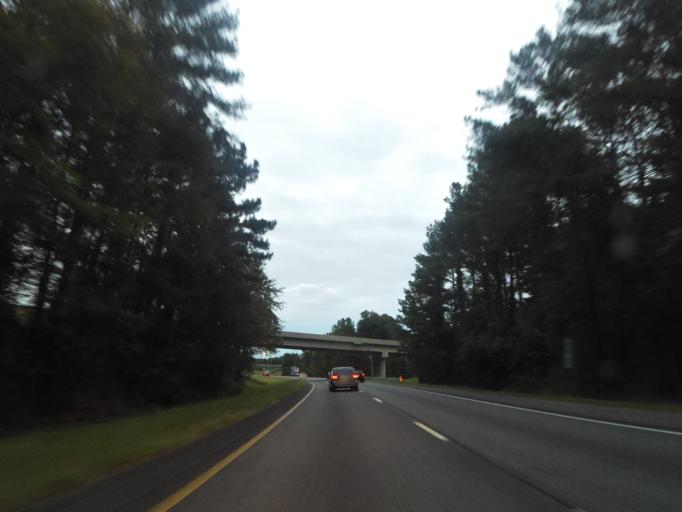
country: US
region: Alabama
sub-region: Etowah County
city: Attalla
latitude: 34.0049
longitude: -86.0801
